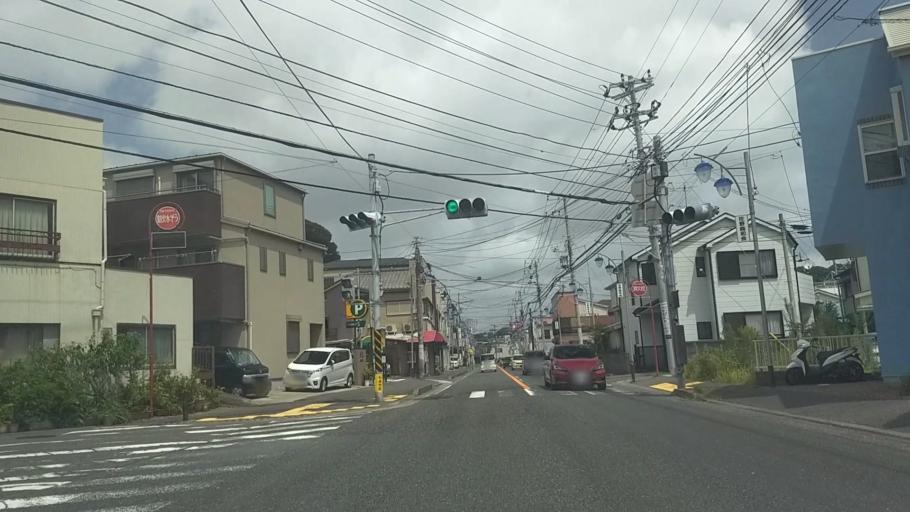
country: JP
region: Kanagawa
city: Yokosuka
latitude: 35.2610
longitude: 139.6688
